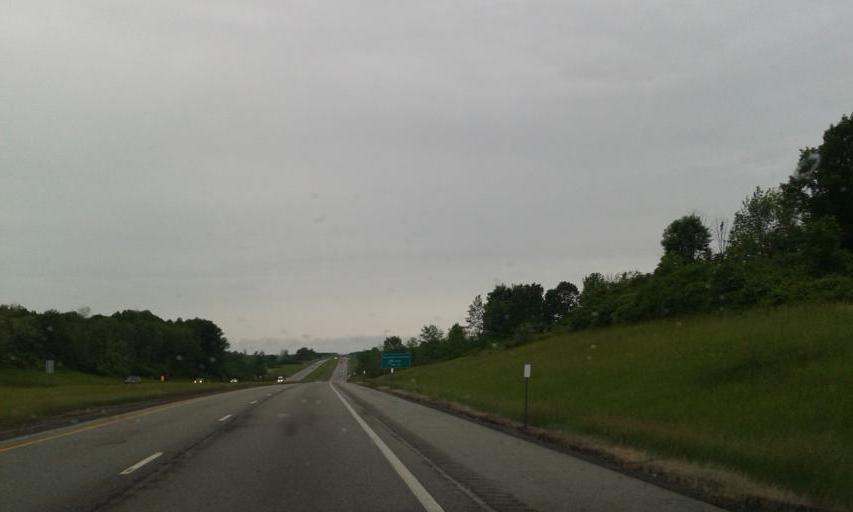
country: US
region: New York
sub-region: Genesee County
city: Bergen
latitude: 43.0286
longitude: -77.9394
